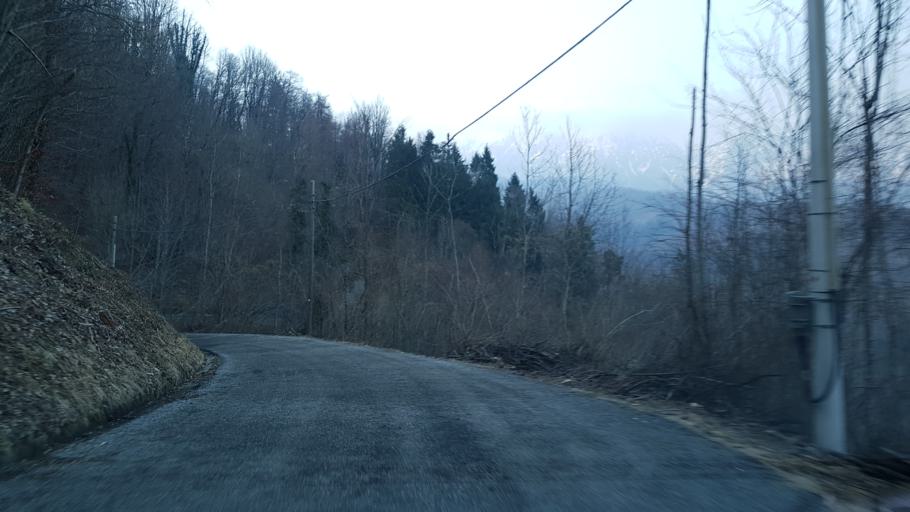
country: IT
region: Friuli Venezia Giulia
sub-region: Provincia di Udine
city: Taipana
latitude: 46.2403
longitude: 13.4036
